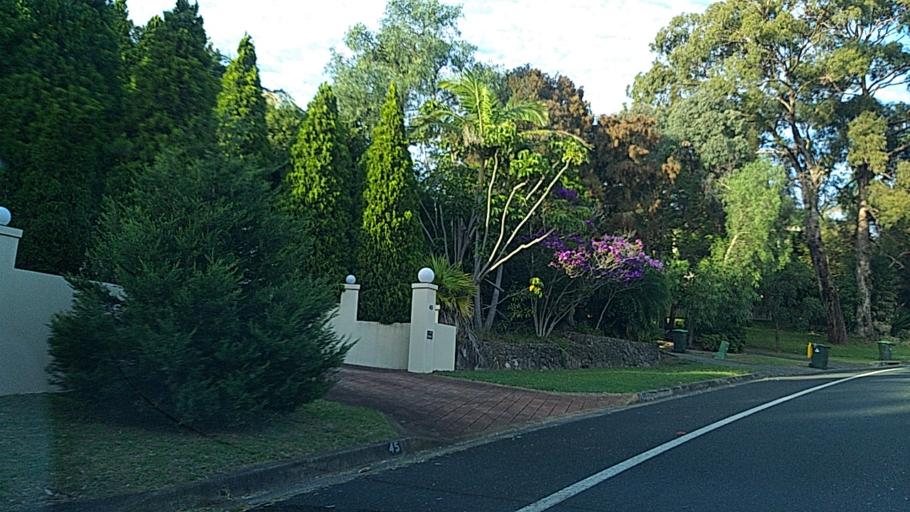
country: AU
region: New South Wales
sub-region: Wollongong
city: Mount Ousley
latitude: -34.3924
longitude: 150.8734
